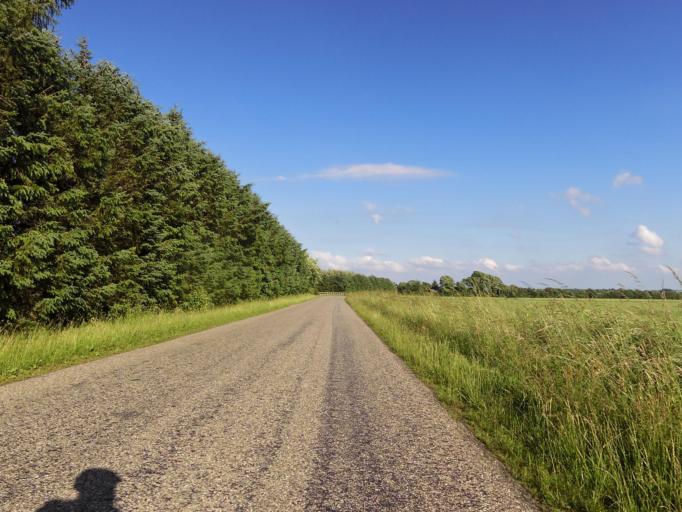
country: DK
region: South Denmark
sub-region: Vejen Kommune
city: Rodding
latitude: 55.3457
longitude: 9.1355
